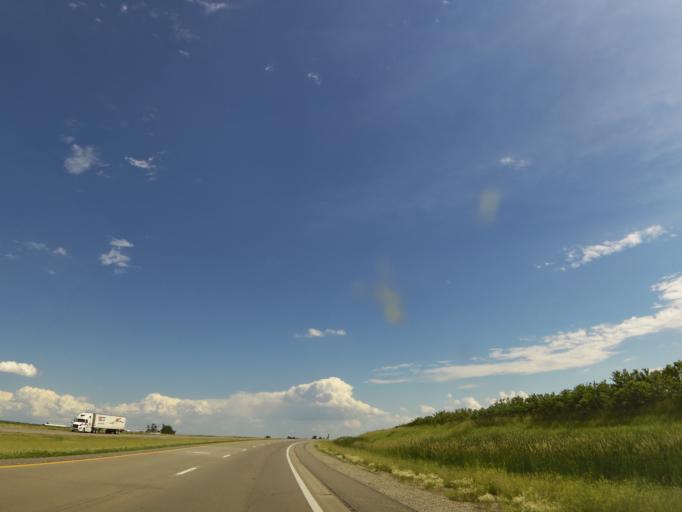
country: US
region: Iowa
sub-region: Henry County
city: Winfield
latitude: 41.2343
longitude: -91.5311
